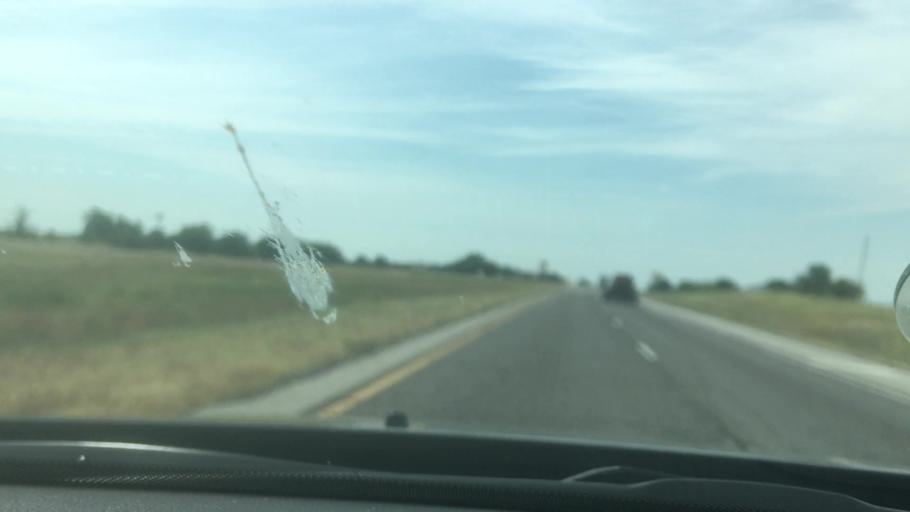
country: US
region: Oklahoma
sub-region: Garvin County
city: Wynnewood
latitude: 34.5619
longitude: -97.1946
